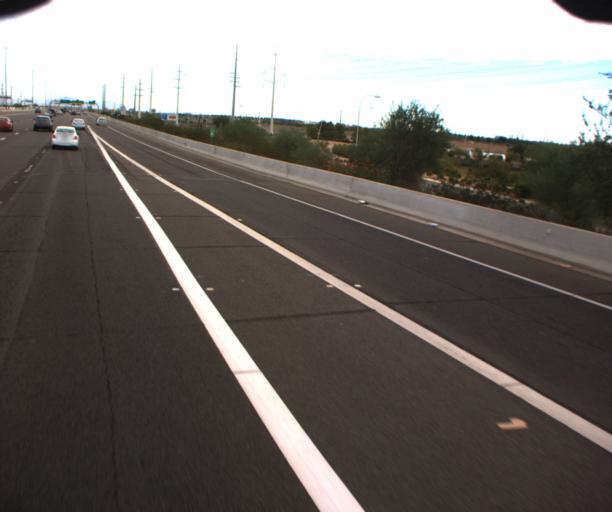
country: US
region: Arizona
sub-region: Maricopa County
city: Tempe
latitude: 33.4359
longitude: -111.9222
